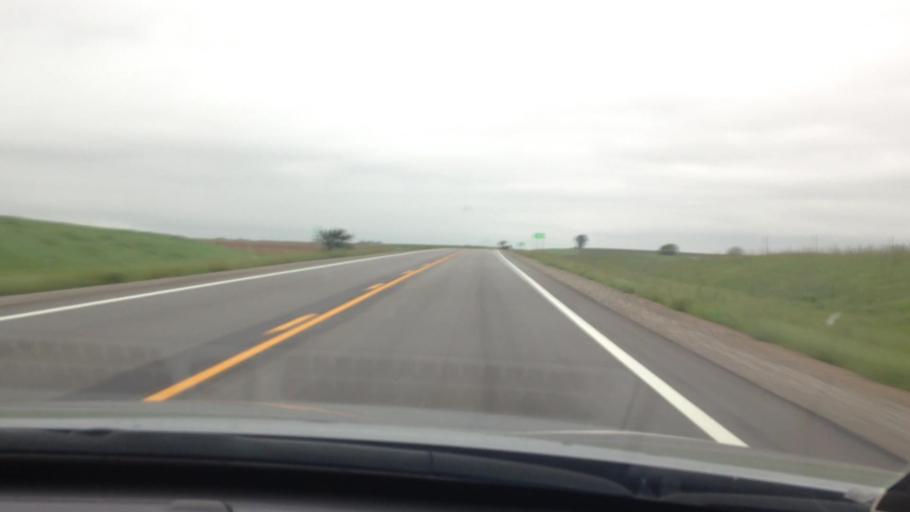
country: US
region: Kansas
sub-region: Brown County
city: Hiawatha
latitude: 39.8413
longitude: -95.4071
